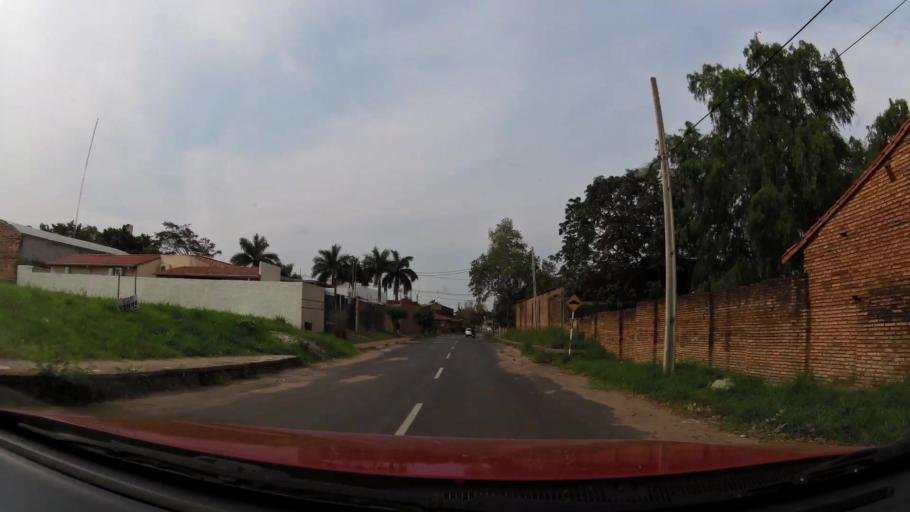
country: PY
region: Central
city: Fernando de la Mora
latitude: -25.2948
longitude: -57.5531
